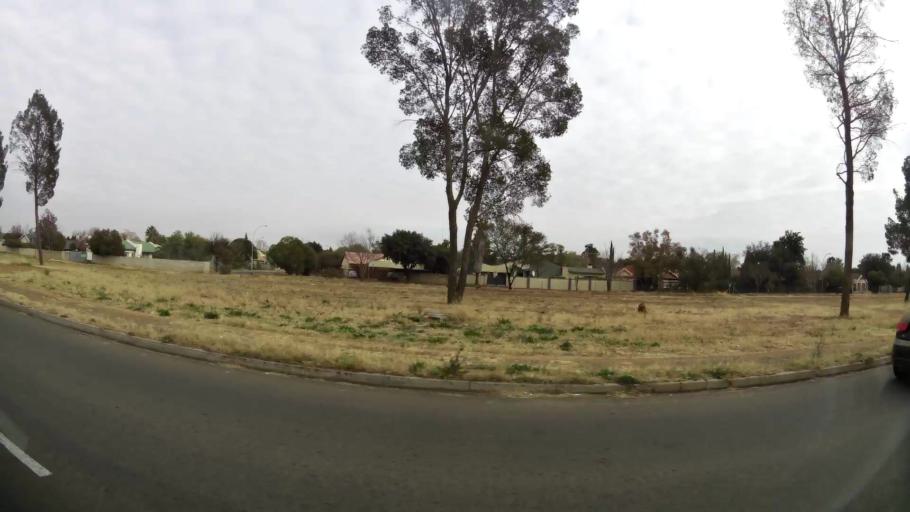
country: ZA
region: Orange Free State
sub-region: Mangaung Metropolitan Municipality
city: Bloemfontein
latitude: -29.1593
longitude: 26.1853
